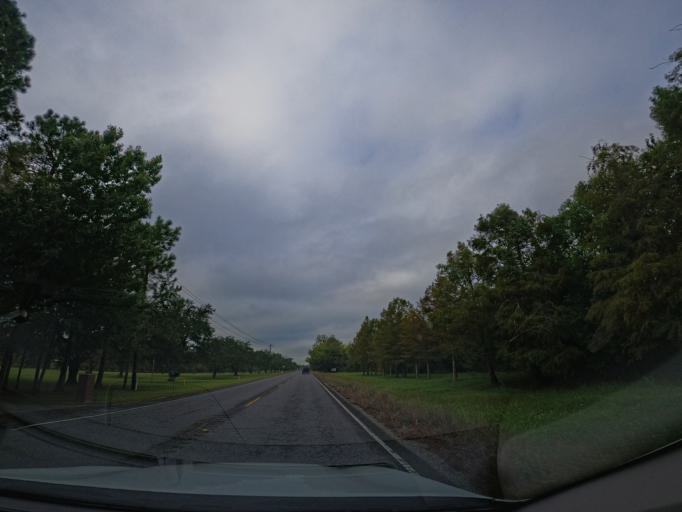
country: US
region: Louisiana
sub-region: Terrebonne Parish
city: Houma
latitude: 29.5649
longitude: -90.7719
